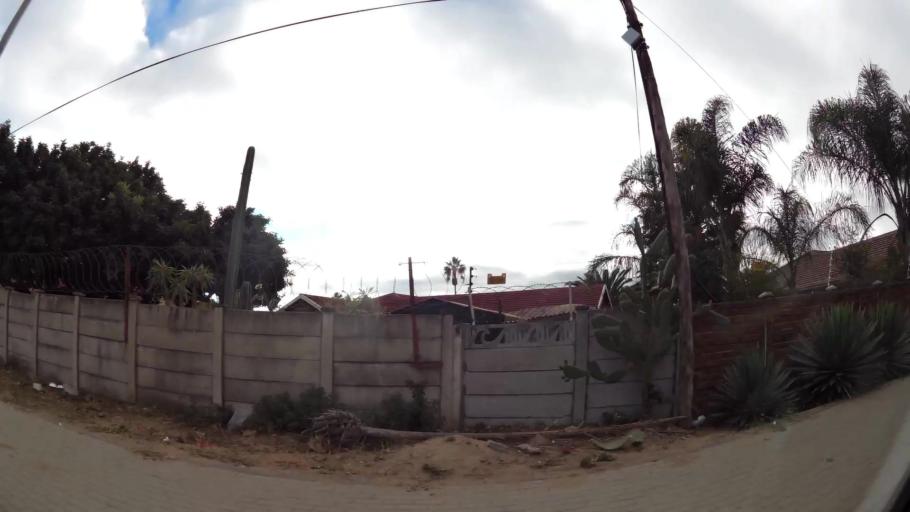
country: ZA
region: Limpopo
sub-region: Capricorn District Municipality
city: Polokwane
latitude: -23.9192
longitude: 29.4466
